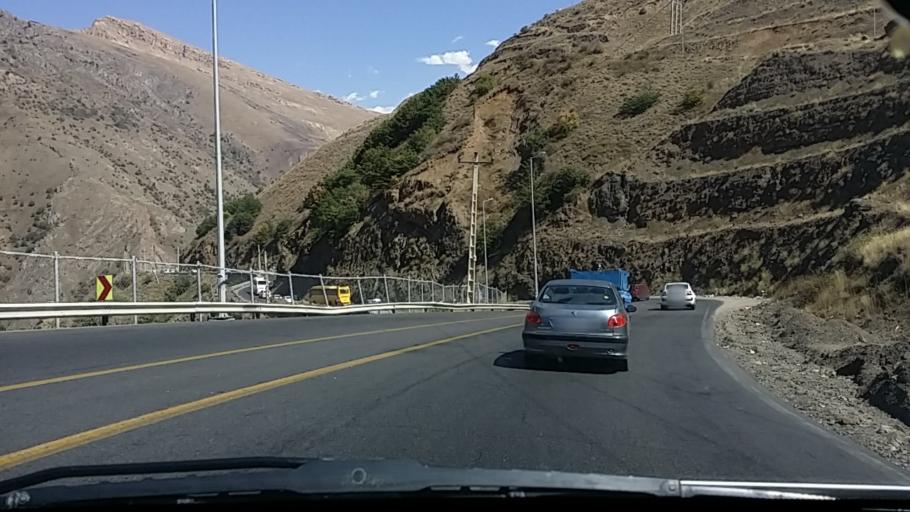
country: IR
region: Tehran
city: Tajrish
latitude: 36.1992
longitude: 51.3235
